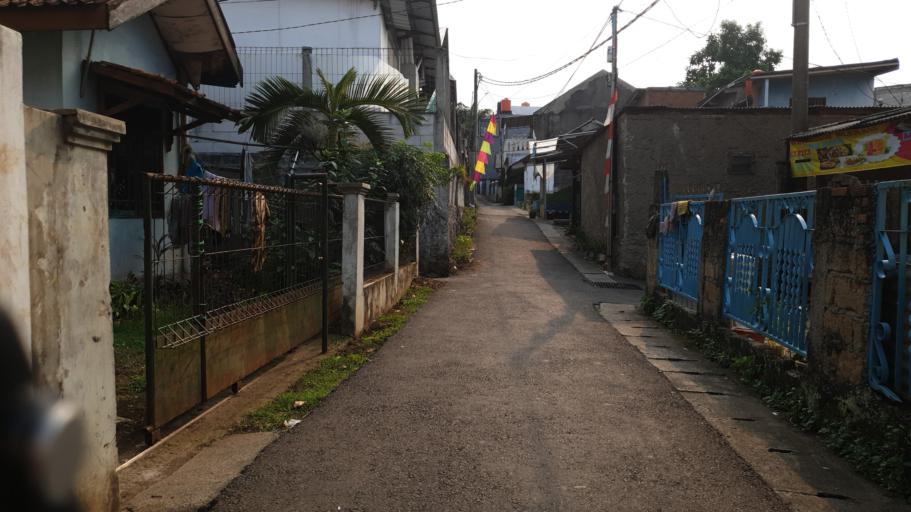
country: ID
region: West Java
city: Depok
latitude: -6.3650
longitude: 106.8356
